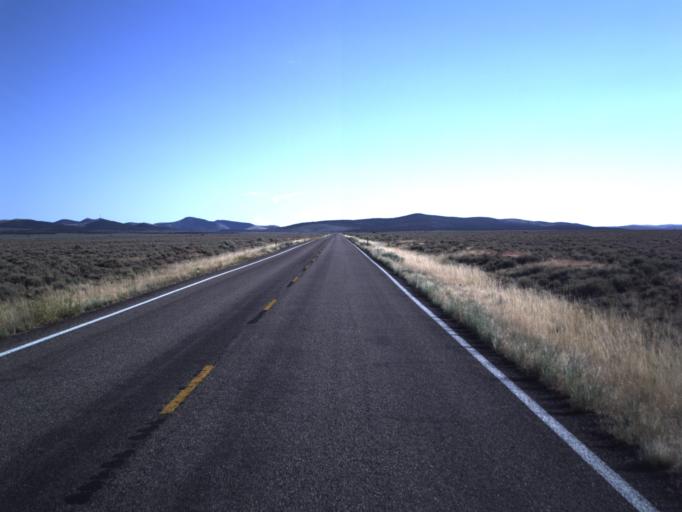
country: US
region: Utah
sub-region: Iron County
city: Enoch
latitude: 37.9764
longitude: -113.0046
